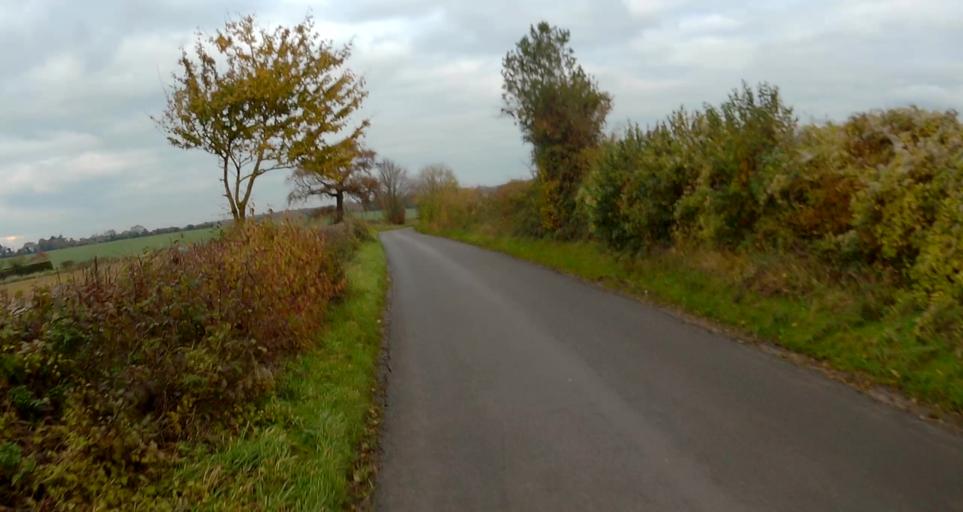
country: GB
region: England
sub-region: Hampshire
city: Long Sutton
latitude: 51.2275
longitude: -0.8759
